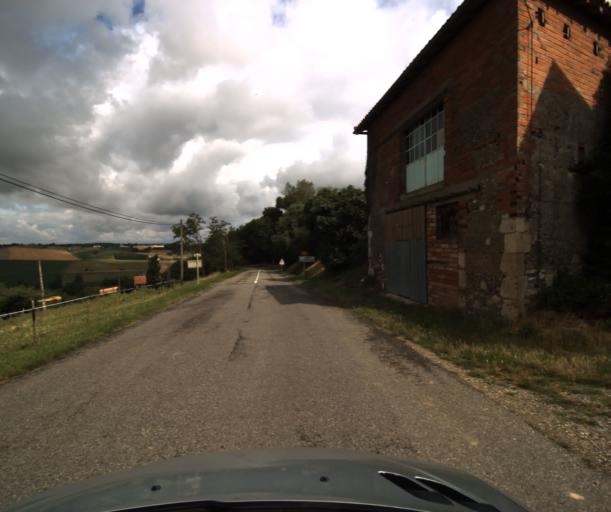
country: FR
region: Midi-Pyrenees
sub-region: Departement du Tarn-et-Garonne
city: Lavit
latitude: 43.9586
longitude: 0.9171
